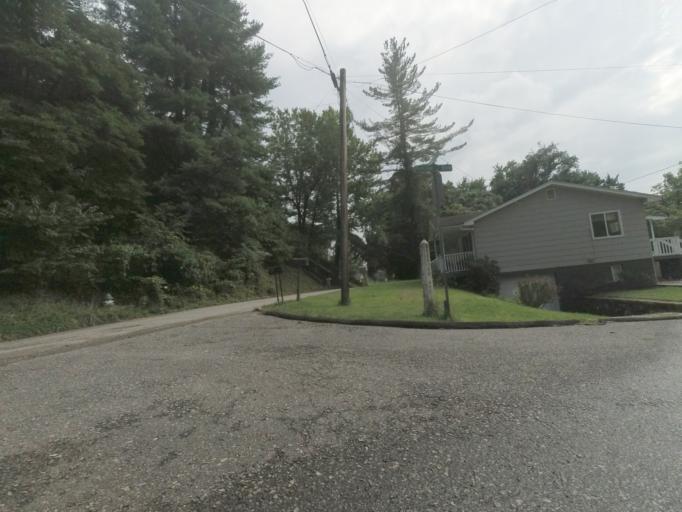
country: US
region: West Virginia
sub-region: Cabell County
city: Huntington
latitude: 38.4025
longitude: -82.4680
